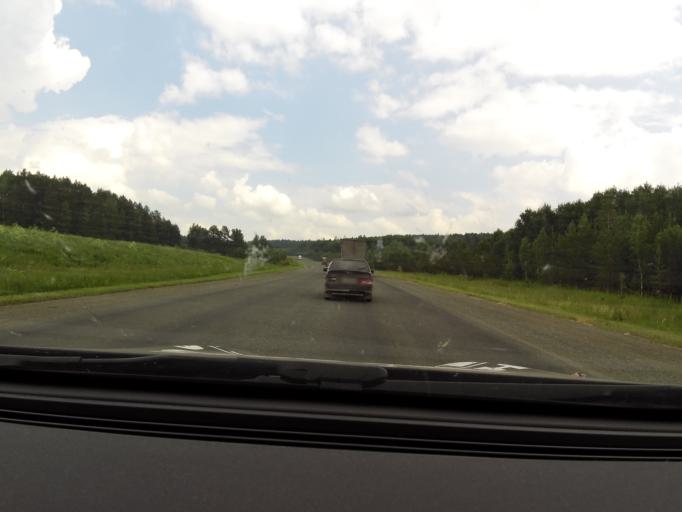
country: RU
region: Sverdlovsk
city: Ufimskiy
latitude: 56.7818
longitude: 58.2841
